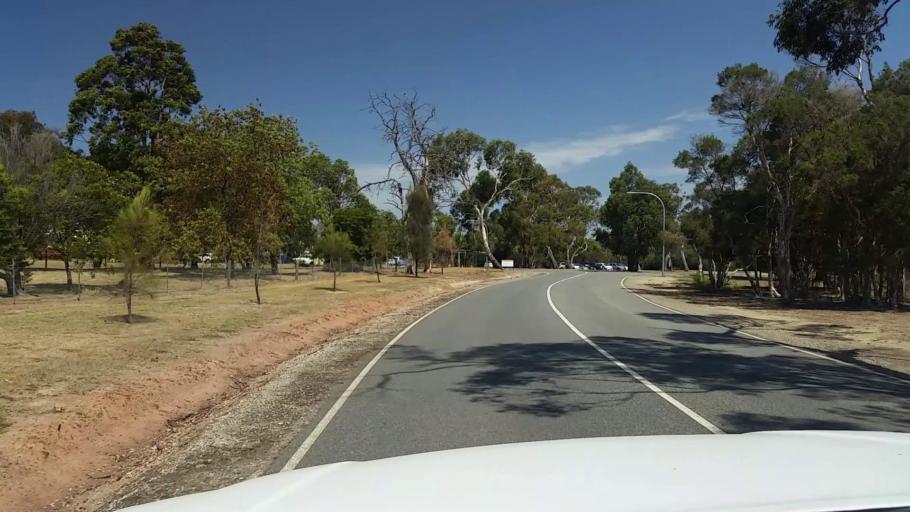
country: AU
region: Victoria
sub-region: Mornington Peninsula
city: Tyabb
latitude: -38.2664
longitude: 145.1917
